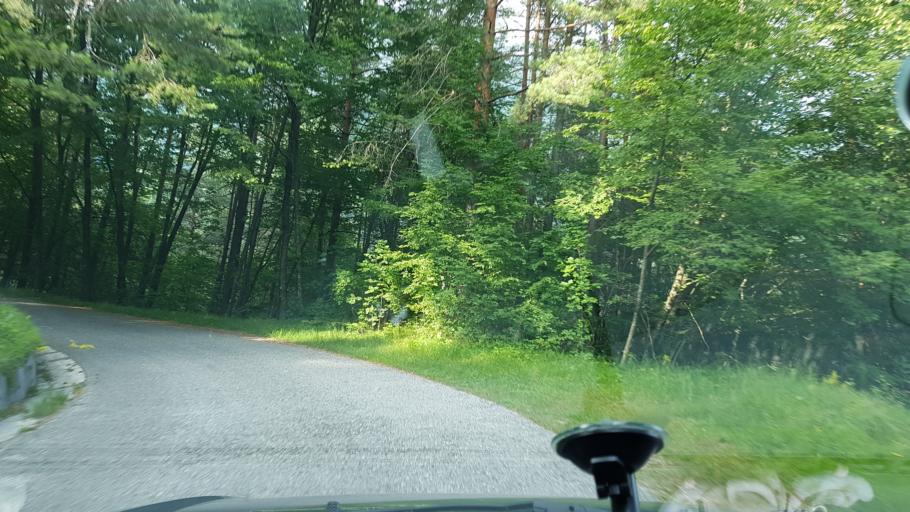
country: IT
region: Friuli Venezia Giulia
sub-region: Provincia di Udine
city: Prato
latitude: 46.3566
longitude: 13.3729
